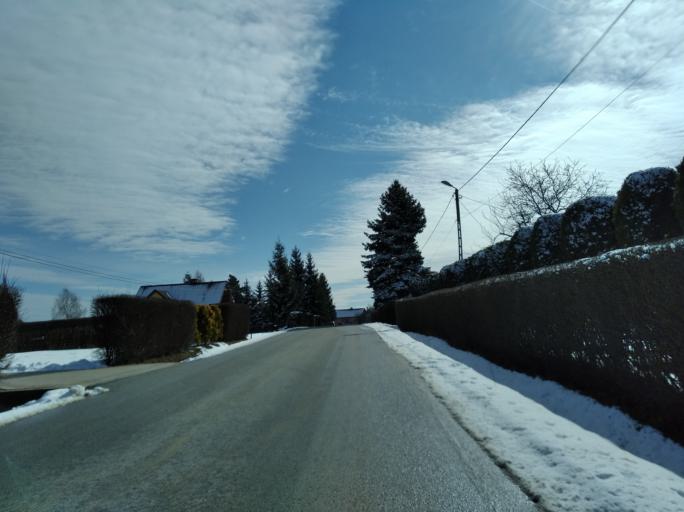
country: PL
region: Subcarpathian Voivodeship
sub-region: Powiat brzozowski
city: Jablonica Polska
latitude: 49.7246
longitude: 21.9032
